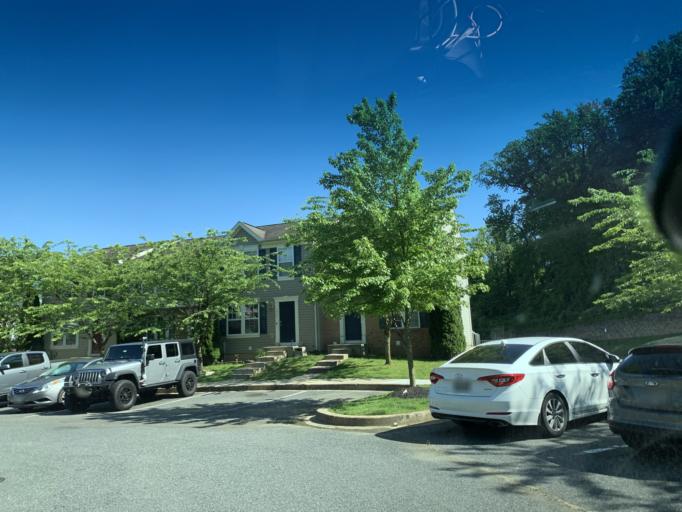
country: US
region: Maryland
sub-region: Harford County
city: Riverside
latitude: 39.4935
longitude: -76.2260
